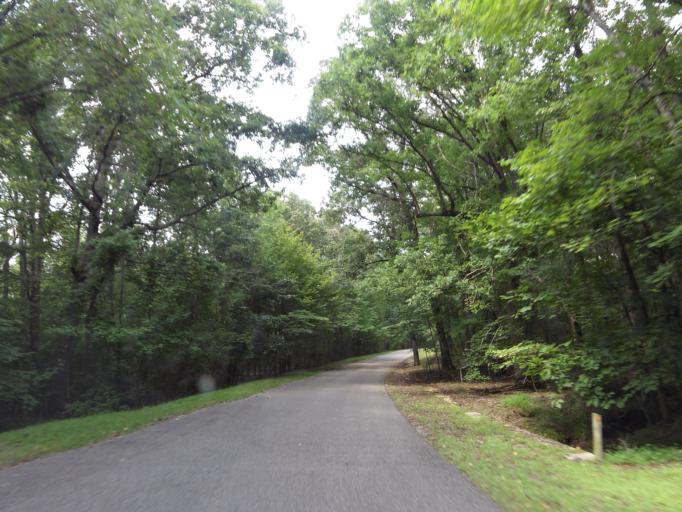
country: US
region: Tennessee
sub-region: Hardin County
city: Crump
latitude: 35.1331
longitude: -88.3398
